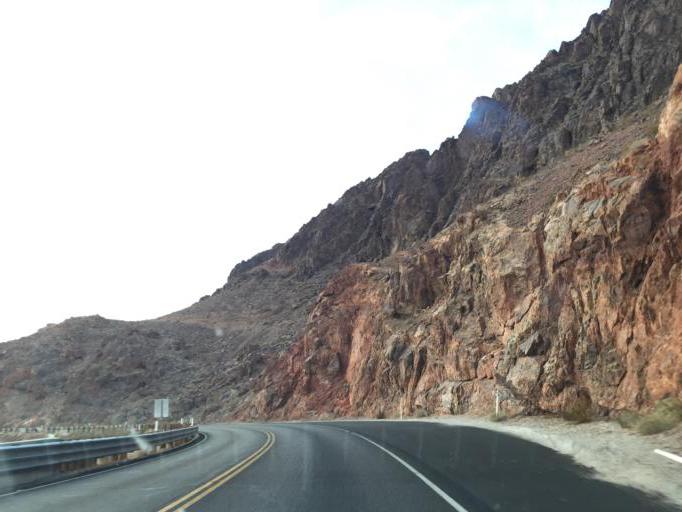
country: US
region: Nevada
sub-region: Clark County
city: Boulder City
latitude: 36.0108
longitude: -114.7659
